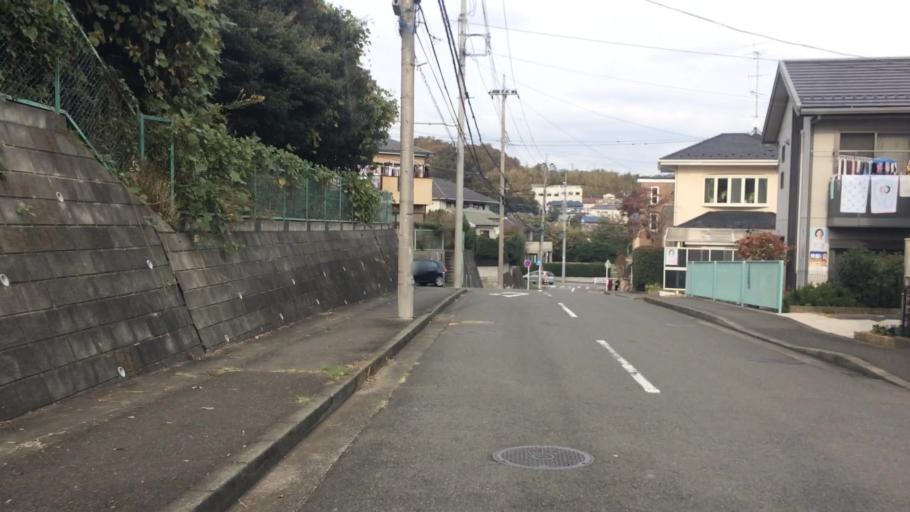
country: JP
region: Tokyo
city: Chofugaoka
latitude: 35.5646
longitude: 139.6002
